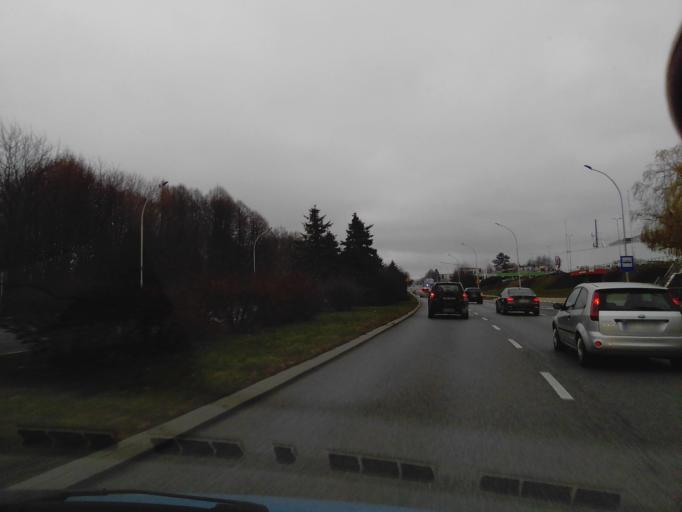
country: PL
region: Subcarpathian Voivodeship
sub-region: Rzeszow
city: Rzeszow
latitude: 50.0400
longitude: 21.9772
